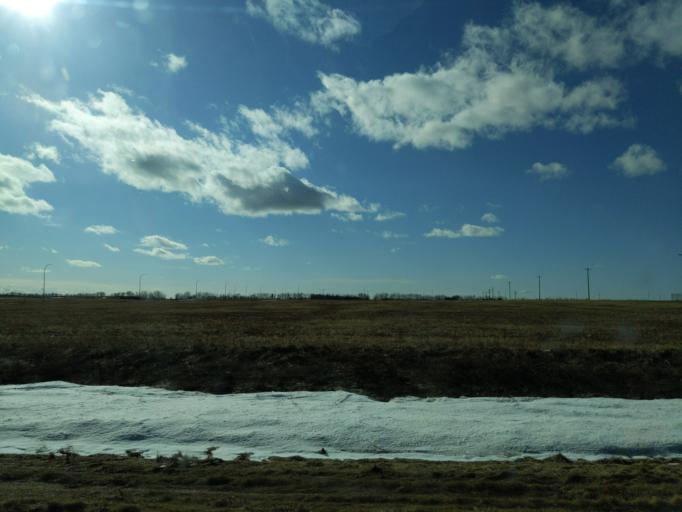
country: CA
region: Saskatchewan
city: Lloydminster
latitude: 53.3008
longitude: -110.0447
